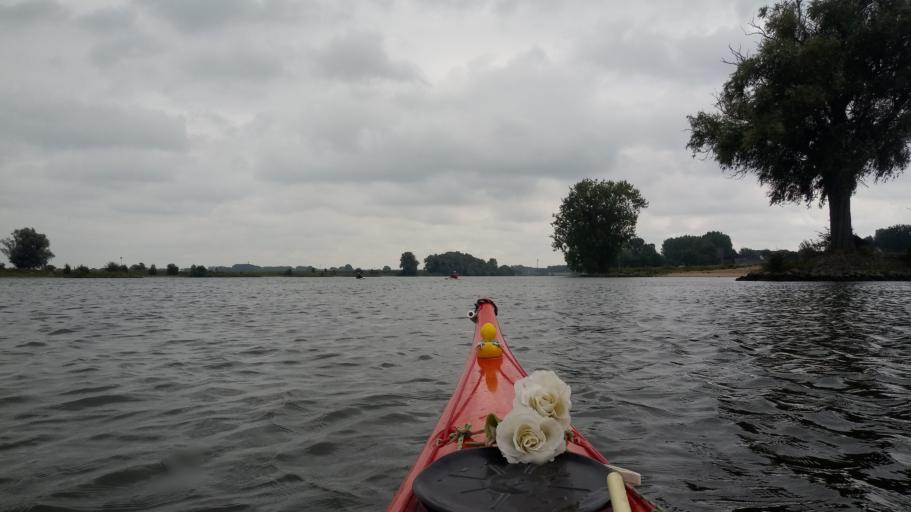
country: NL
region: Gelderland
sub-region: Gemeente Maasdriel
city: Hedel
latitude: 51.7411
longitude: 5.2301
